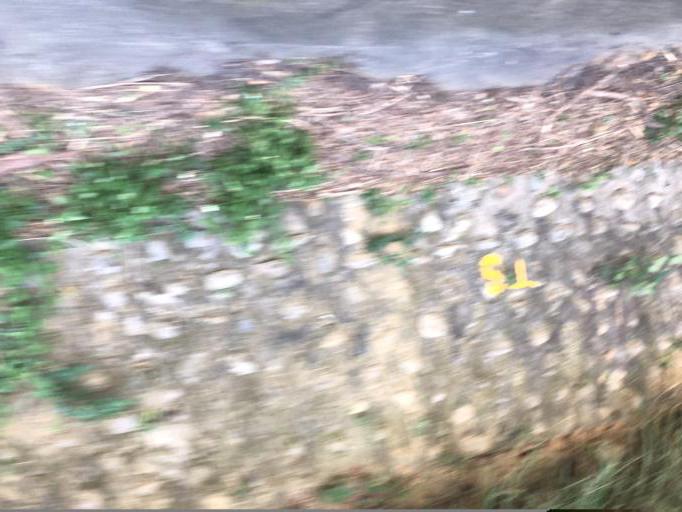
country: TW
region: Taiwan
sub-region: Hsinchu
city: Hsinchu
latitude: 24.7525
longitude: 120.9811
